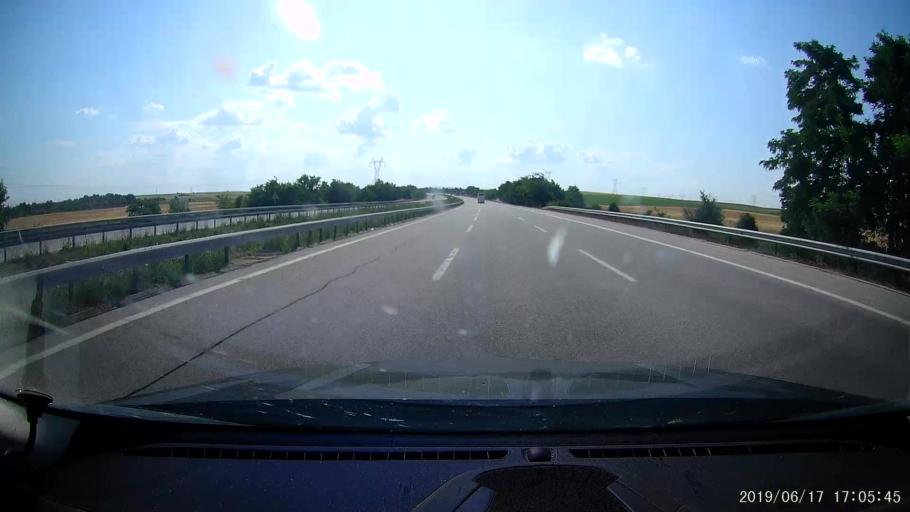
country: TR
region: Edirne
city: Edirne
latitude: 41.6617
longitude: 26.6904
